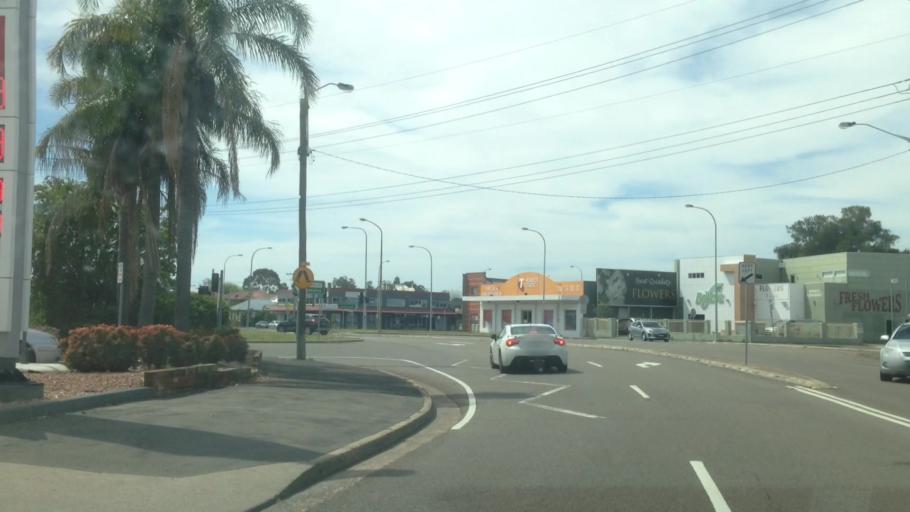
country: AU
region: New South Wales
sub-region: Newcastle
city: Broadmeadow
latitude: -32.9252
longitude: 151.7367
